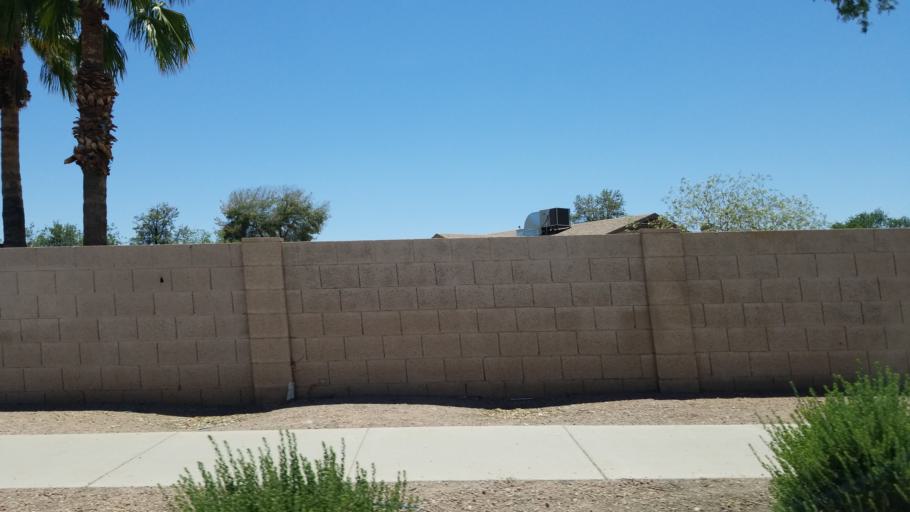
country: US
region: Arizona
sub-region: Maricopa County
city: Tolleson
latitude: 33.5087
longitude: -112.2488
